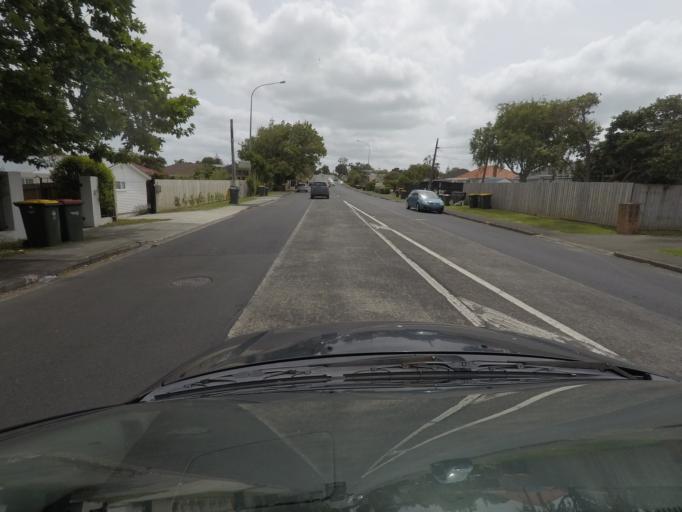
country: NZ
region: Auckland
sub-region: Auckland
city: Pakuranga
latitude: -36.8953
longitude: 174.9227
